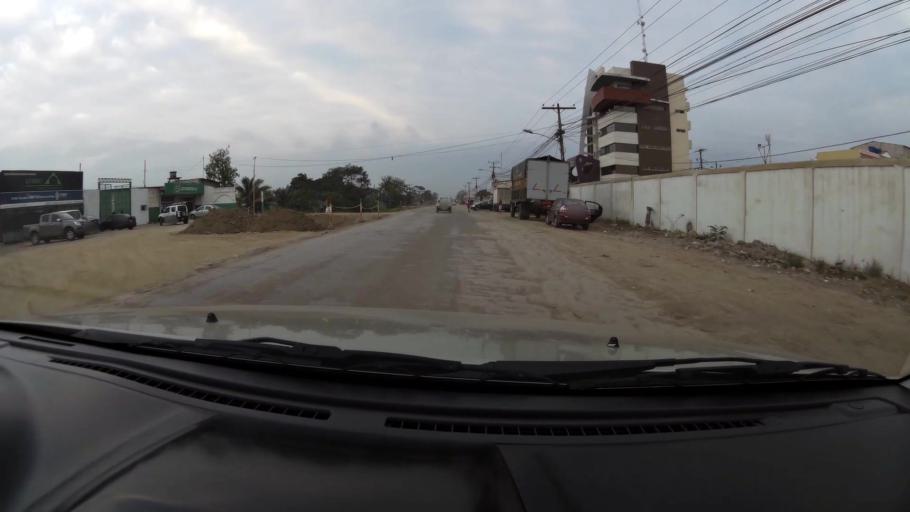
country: EC
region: El Oro
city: Machala
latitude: -3.2718
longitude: -79.9315
